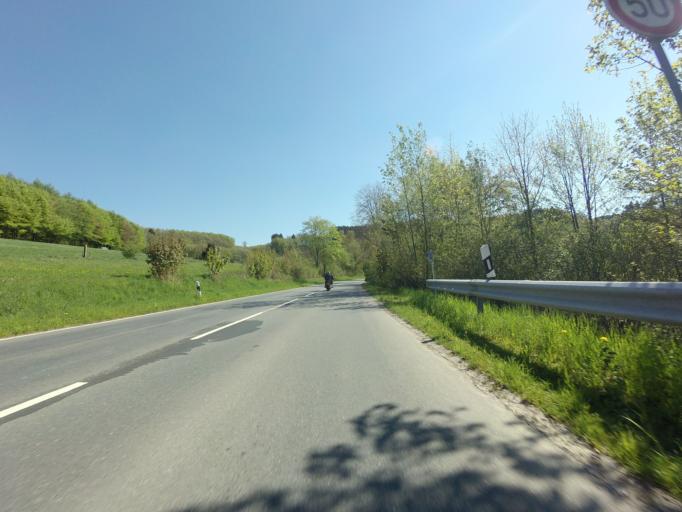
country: DE
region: North Rhine-Westphalia
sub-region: Regierungsbezirk Arnsberg
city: Olpe
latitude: 51.0980
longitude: 7.8339
